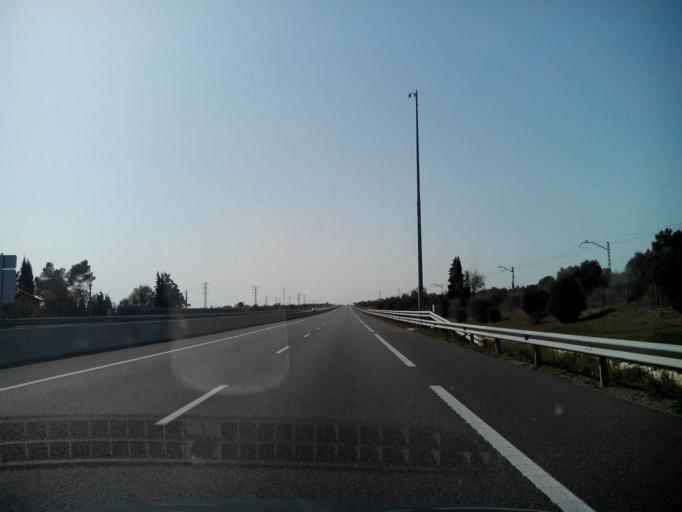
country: ES
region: Catalonia
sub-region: Provincia de Tarragona
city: Alcover
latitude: 41.2412
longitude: 1.1672
